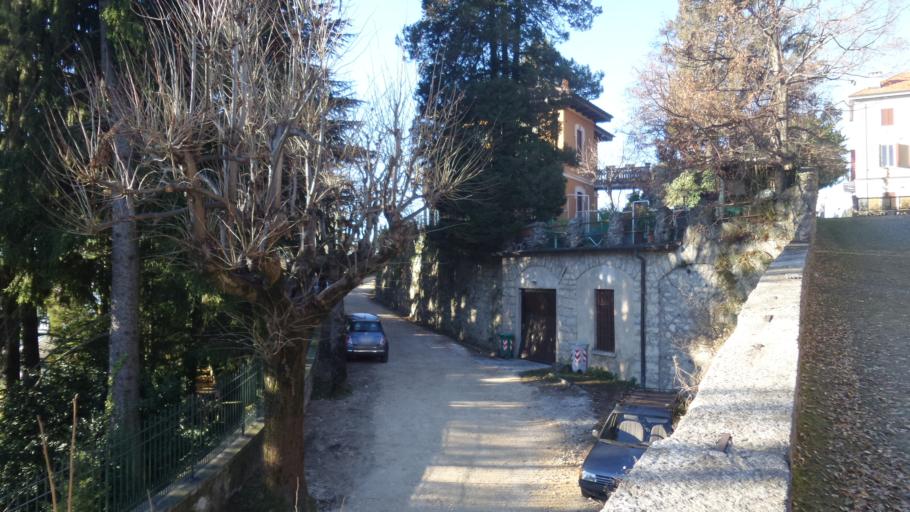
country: IT
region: Lombardy
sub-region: Provincia di Varese
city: Casciago
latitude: 45.8531
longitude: 8.7953
